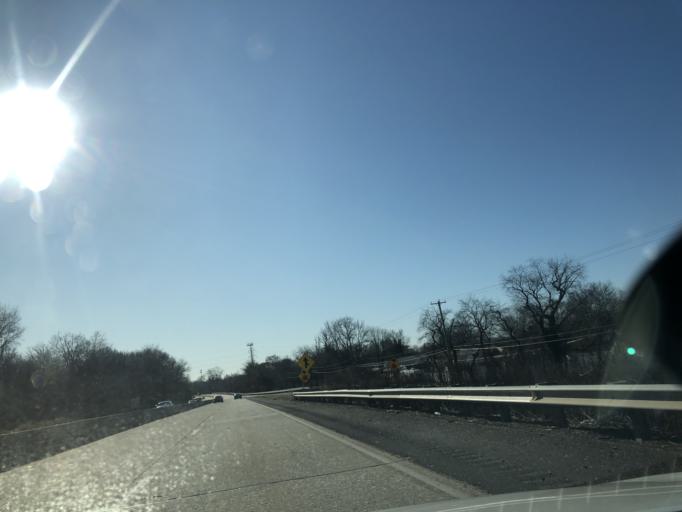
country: US
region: Pennsylvania
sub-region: Bucks County
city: Levittown
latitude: 40.1710
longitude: -74.8125
